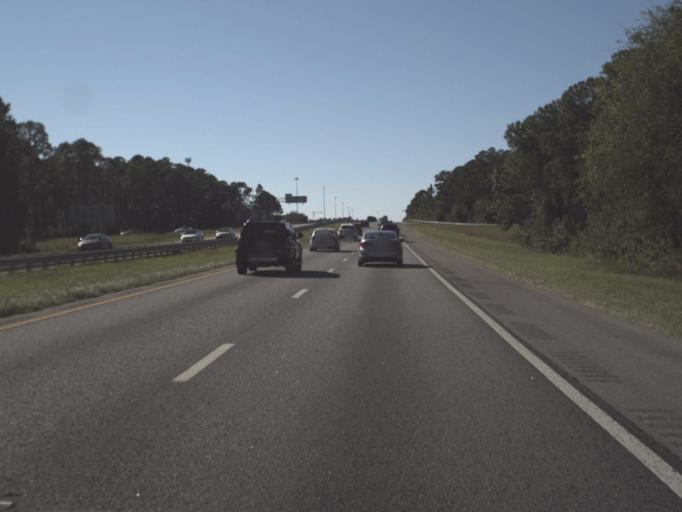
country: US
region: Florida
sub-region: Orange County
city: Williamsburg
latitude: 28.4212
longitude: -81.4556
